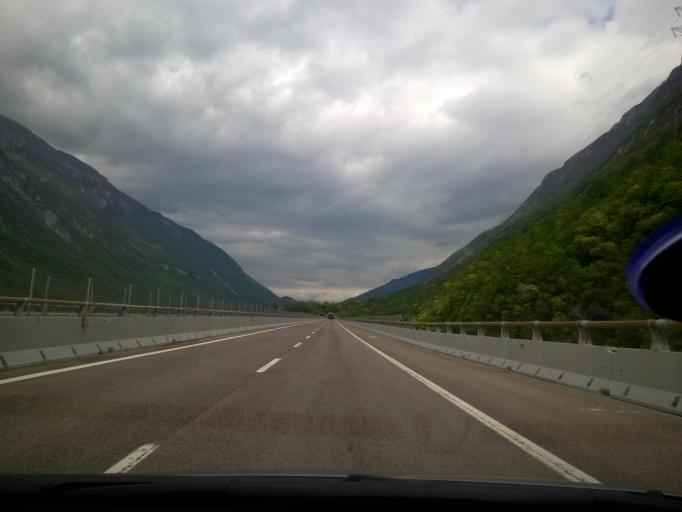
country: IT
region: Veneto
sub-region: Provincia di Treviso
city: Fregona
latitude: 46.0346
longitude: 12.3081
